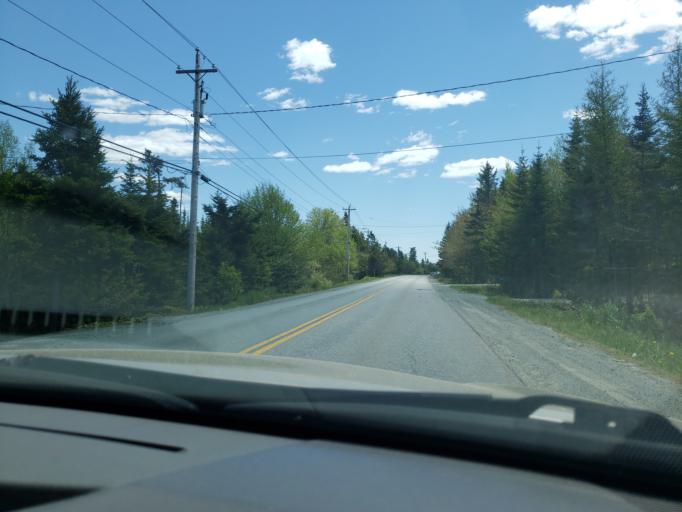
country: CA
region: Nova Scotia
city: Cole Harbour
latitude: 44.7319
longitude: -63.3080
